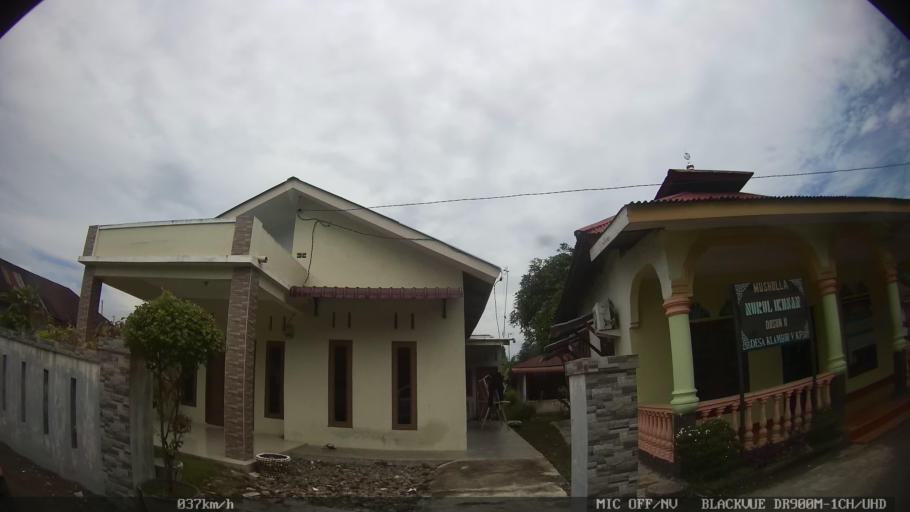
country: ID
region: North Sumatra
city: Sunggal
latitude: 3.6442
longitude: 98.5919
